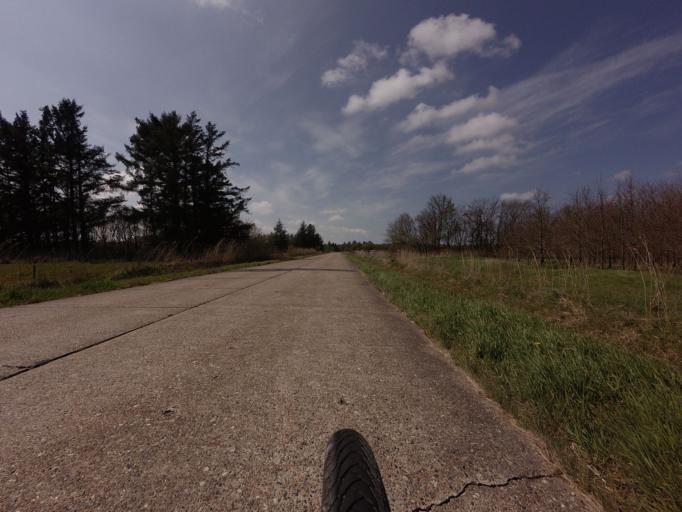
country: DK
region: North Denmark
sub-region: Jammerbugt Kommune
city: Brovst
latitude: 57.1644
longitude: 9.4940
